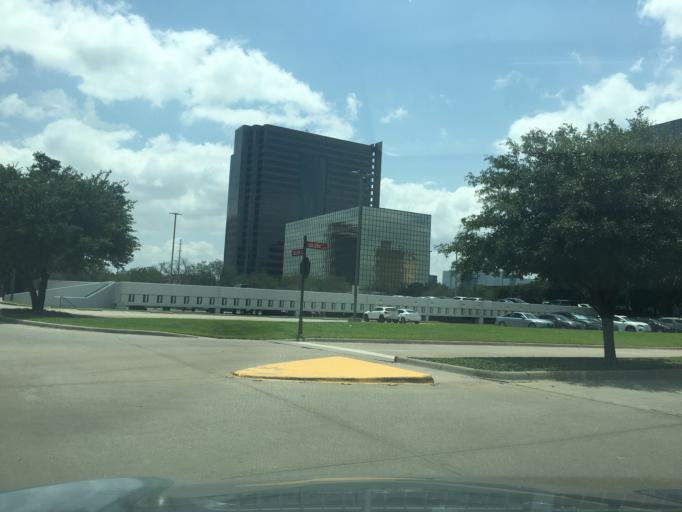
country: US
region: Texas
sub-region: Dallas County
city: Addison
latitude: 32.9293
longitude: -96.8253
